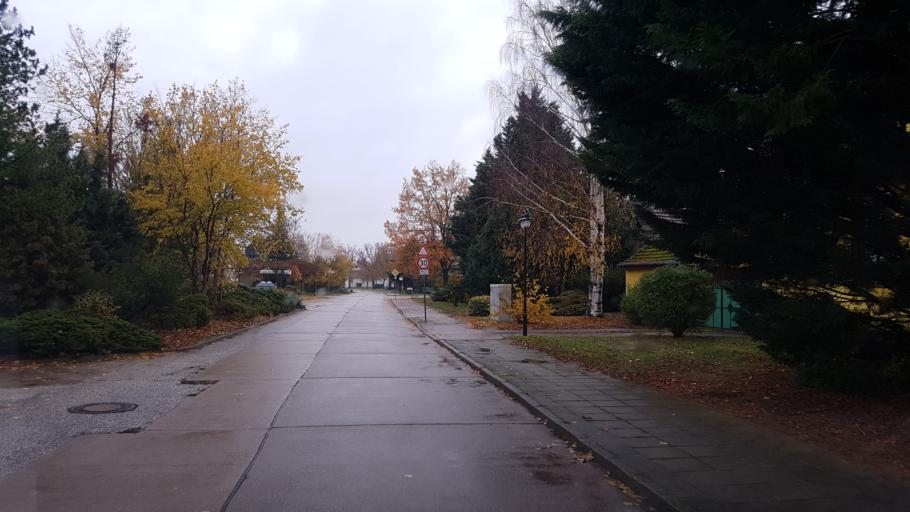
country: DE
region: Brandenburg
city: Herzberg
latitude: 51.6573
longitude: 13.2234
